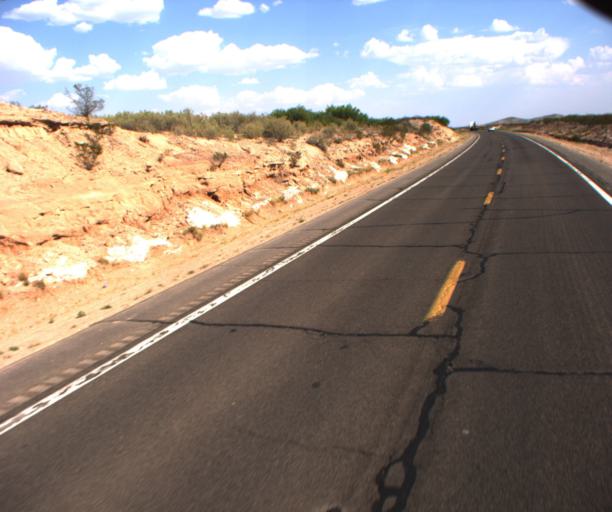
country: US
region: Arizona
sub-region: Greenlee County
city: Clifton
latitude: 32.7836
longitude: -109.1588
